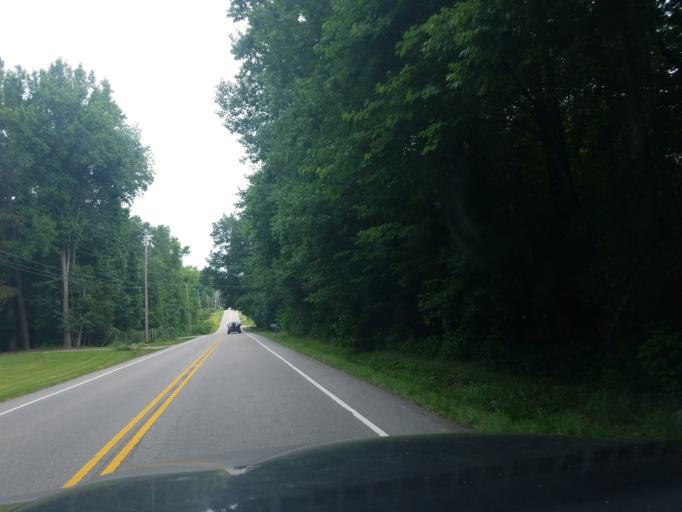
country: US
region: North Carolina
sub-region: Durham County
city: Durham
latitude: 36.1285
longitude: -78.9458
